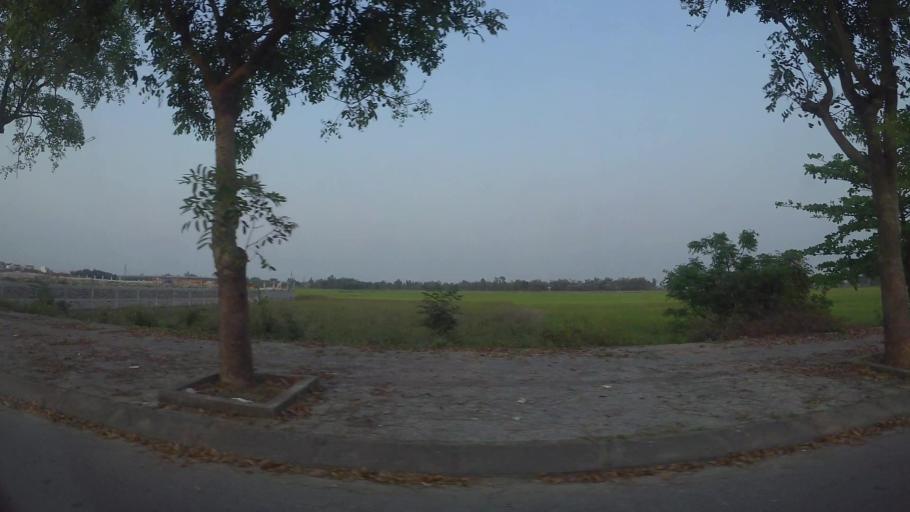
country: VN
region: Da Nang
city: Cam Le
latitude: 15.9624
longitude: 108.2132
